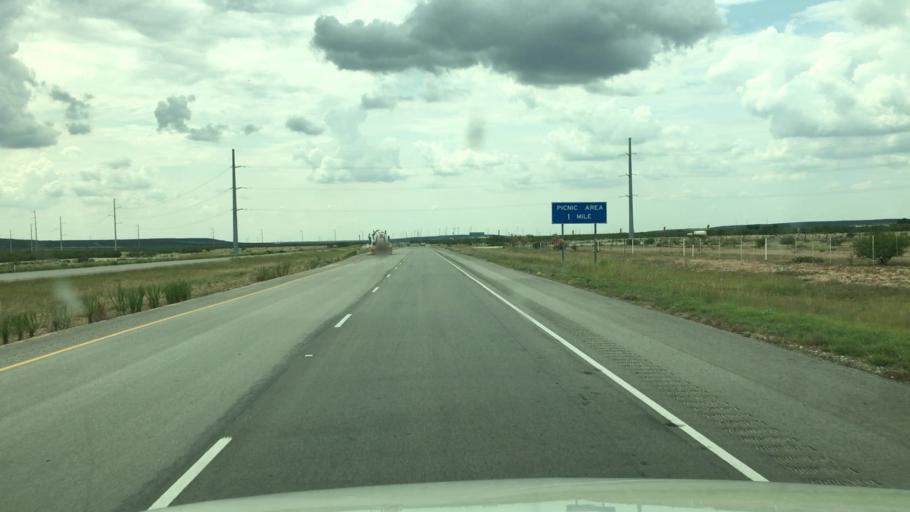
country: US
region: Texas
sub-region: Sterling County
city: Sterling City
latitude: 31.9602
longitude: -101.2108
